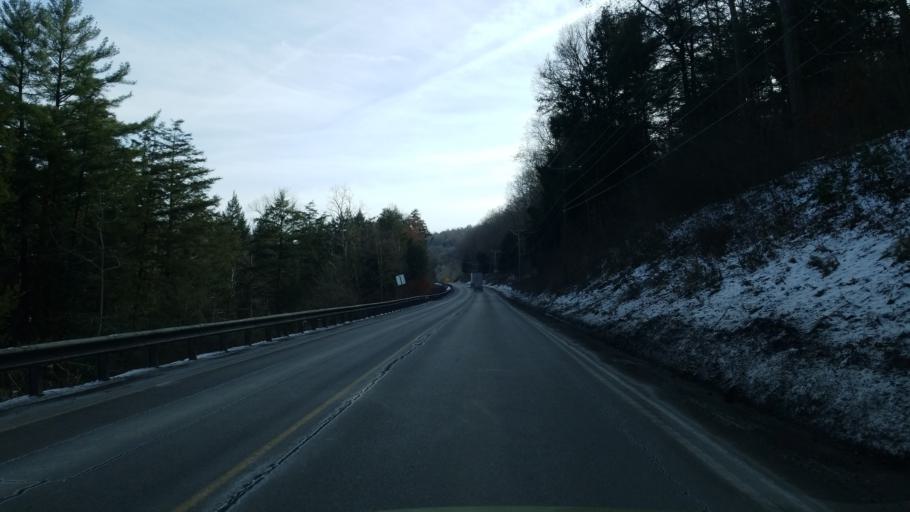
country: US
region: Pennsylvania
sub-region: Clearfield County
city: Treasure Lake
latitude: 41.2039
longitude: -78.5676
